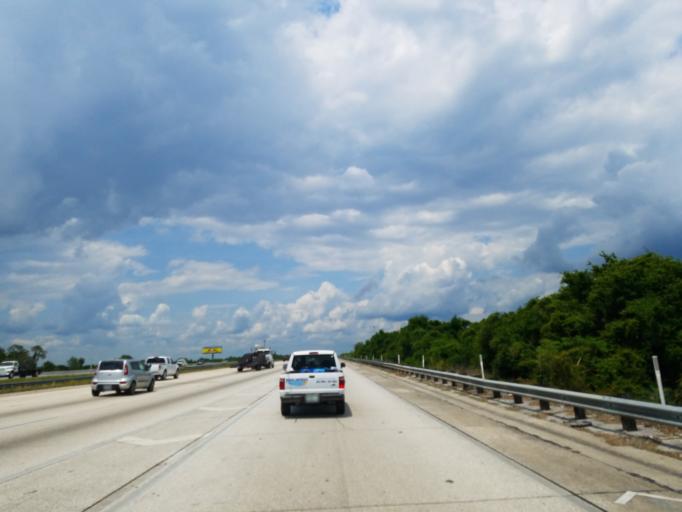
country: US
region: Florida
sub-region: Hillsborough County
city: Mango
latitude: 27.9459
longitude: -82.3284
